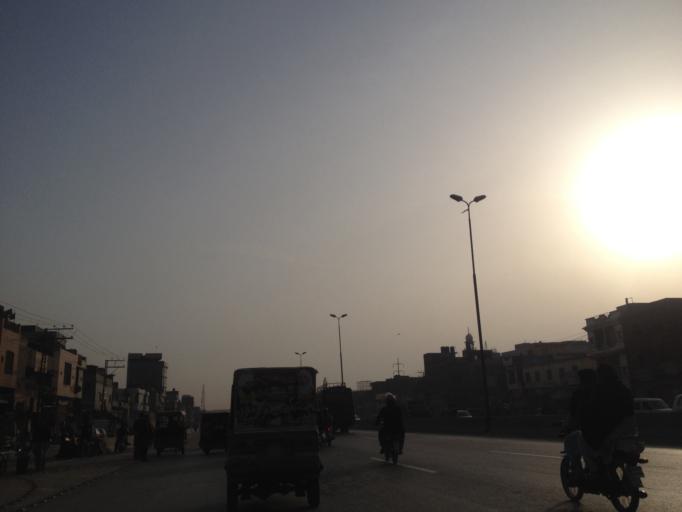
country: PK
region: Punjab
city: Lahore
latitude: 31.5653
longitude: 74.2812
